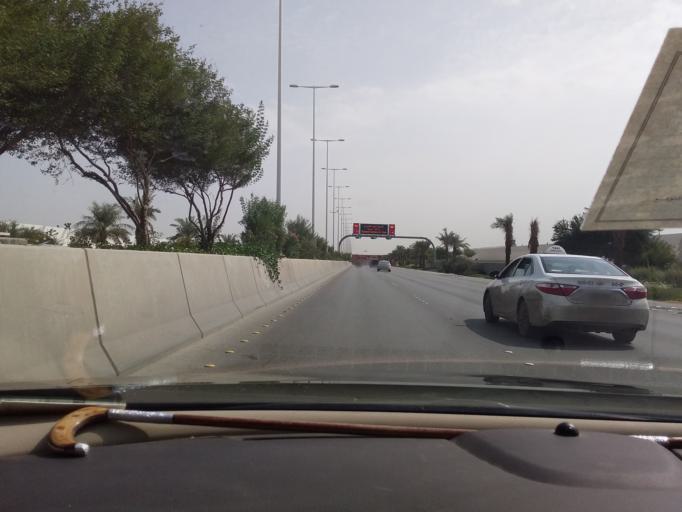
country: SA
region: Ar Riyad
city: Riyadh
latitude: 24.7152
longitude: 46.7168
